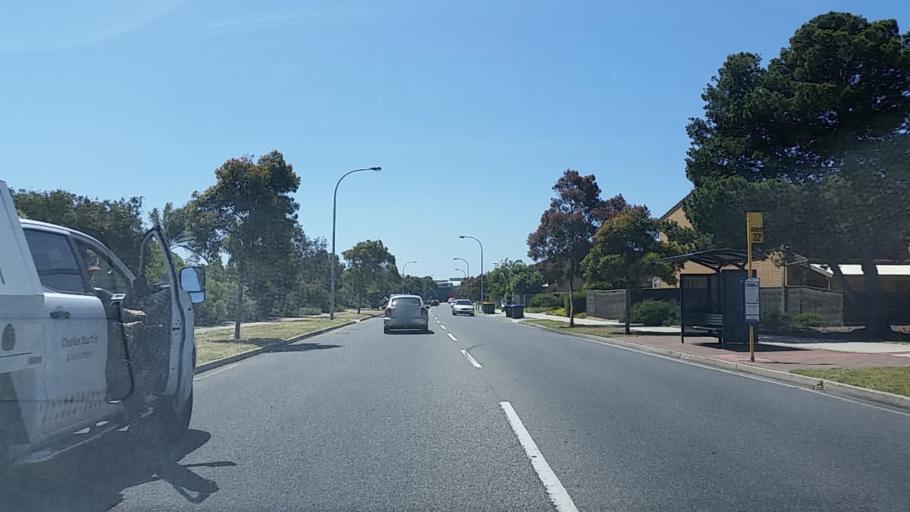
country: AU
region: South Australia
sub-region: Charles Sturt
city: Grange
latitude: -34.8846
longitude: 138.4916
